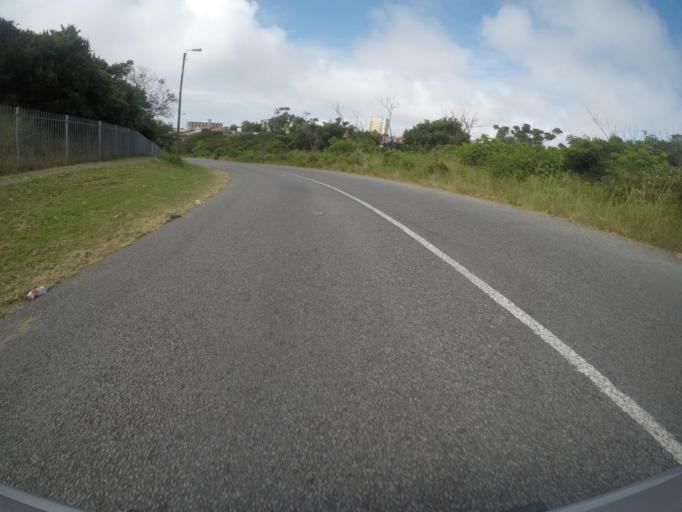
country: ZA
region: Eastern Cape
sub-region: Buffalo City Metropolitan Municipality
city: East London
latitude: -32.9966
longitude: 27.9110
